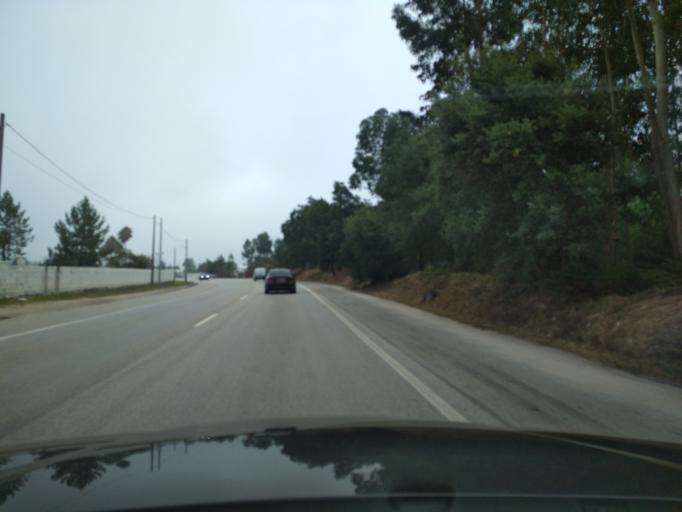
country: PT
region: Aveiro
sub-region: Mealhada
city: Pampilhosa do Botao
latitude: 40.3307
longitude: -8.4511
